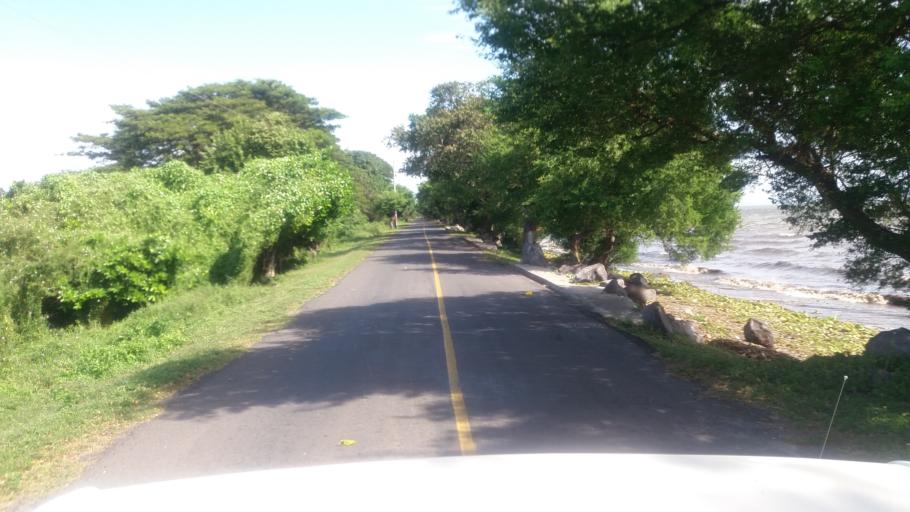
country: NI
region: Granada
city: Granada
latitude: 11.9761
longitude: -85.9421
